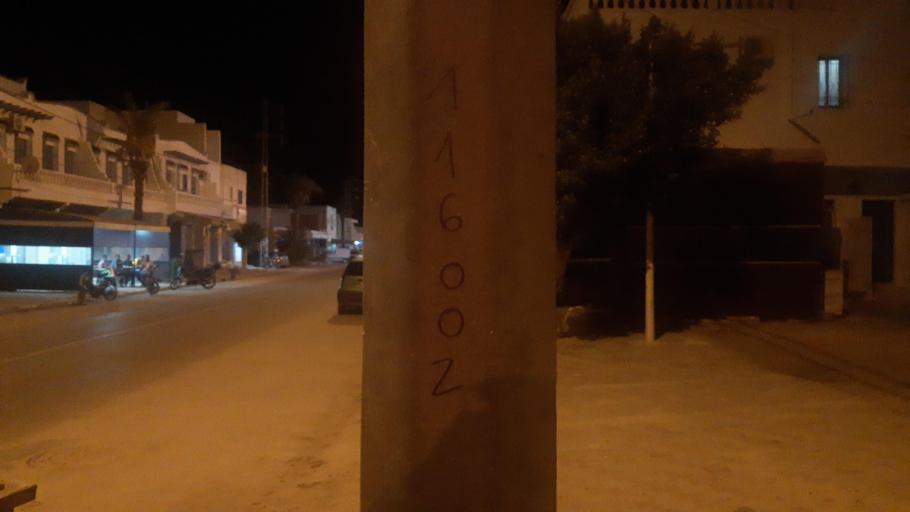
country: TN
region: Madanin
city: Houmt Souk
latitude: 33.7218
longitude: 10.7457
